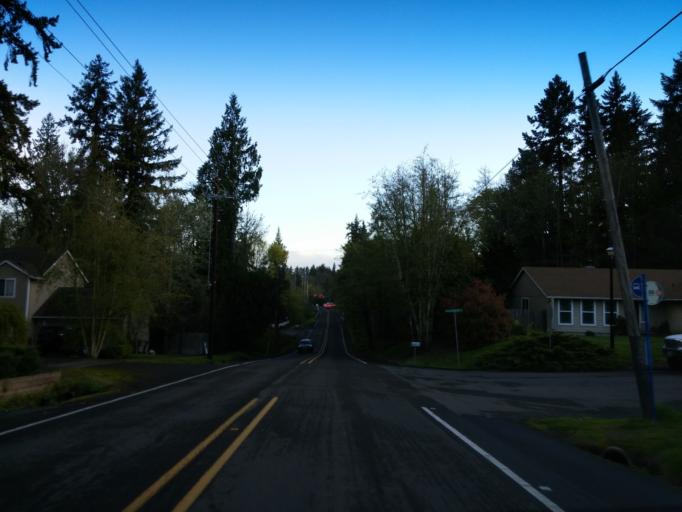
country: US
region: Oregon
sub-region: Washington County
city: Aloha
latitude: 45.5122
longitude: -122.8795
